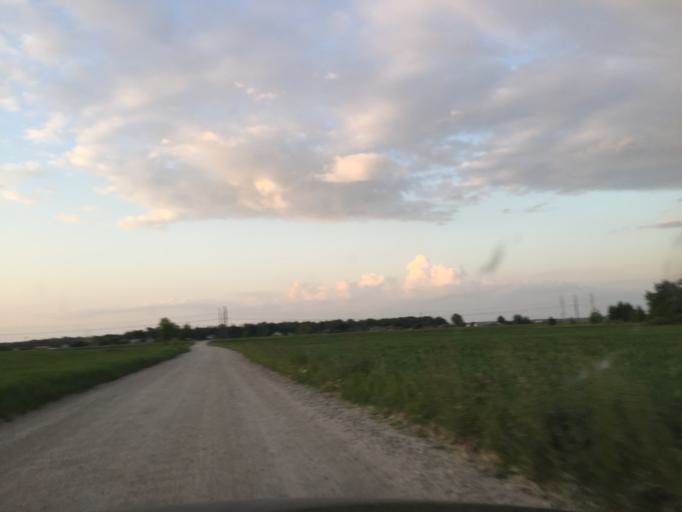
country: LT
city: Kursenai
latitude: 56.0107
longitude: 22.9557
